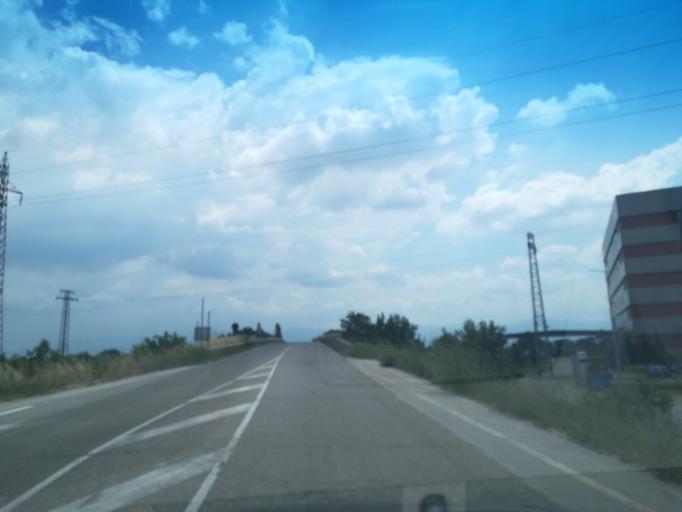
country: BG
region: Plovdiv
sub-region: Obshtina Plovdiv
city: Plovdiv
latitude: 42.1923
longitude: 24.6764
